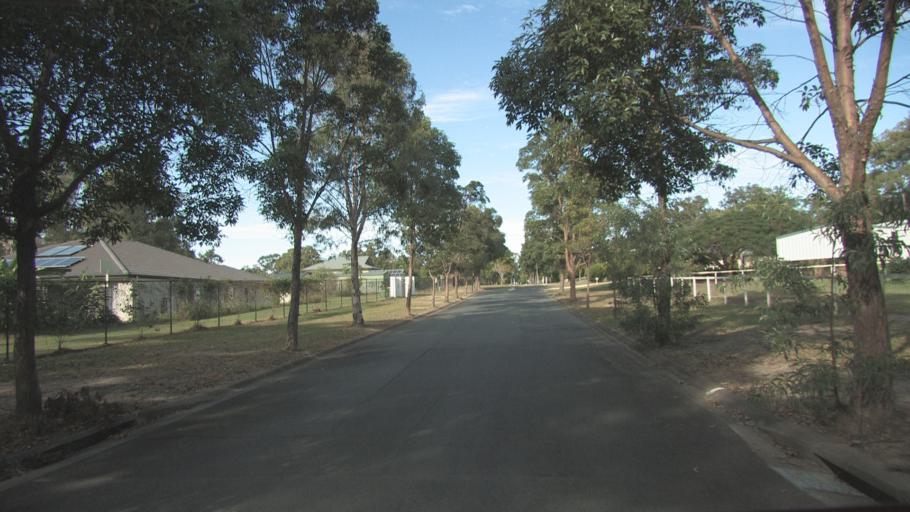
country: AU
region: Queensland
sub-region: Brisbane
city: Forest Lake
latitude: -27.6600
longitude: 153.0162
